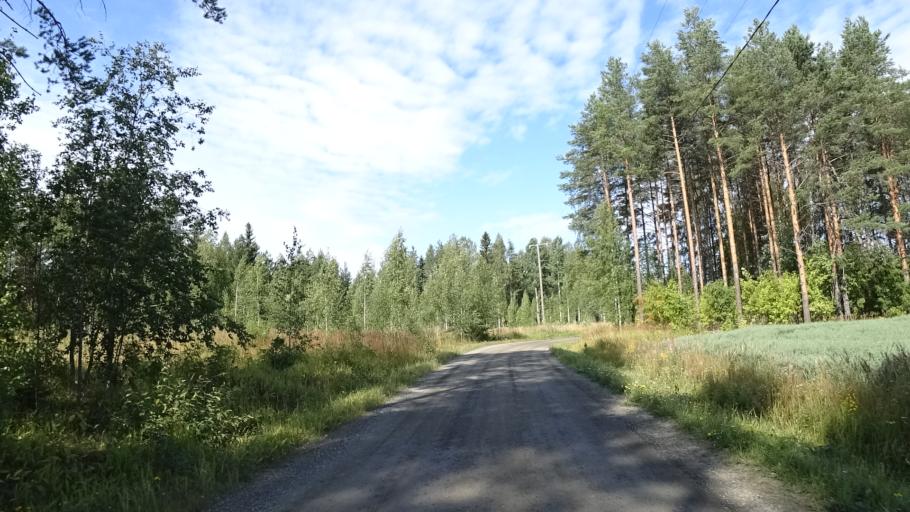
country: FI
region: North Karelia
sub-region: Joensuu
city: Pyhaeselkae
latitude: 62.3709
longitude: 29.8392
